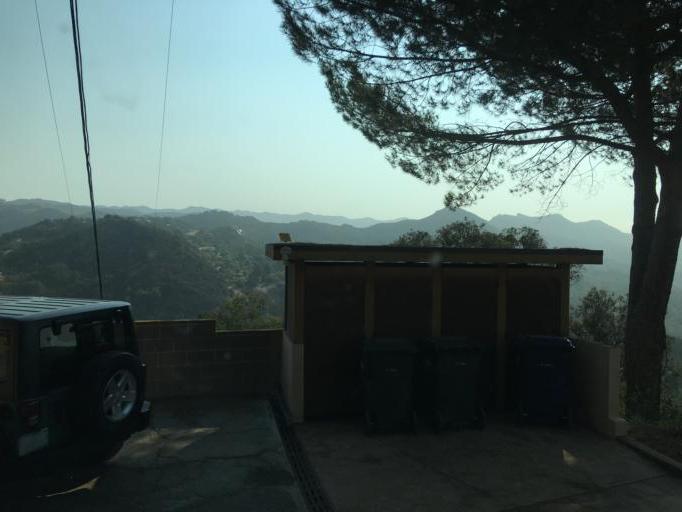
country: US
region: California
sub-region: Los Angeles County
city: Topanga
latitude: 34.0827
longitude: -118.6056
